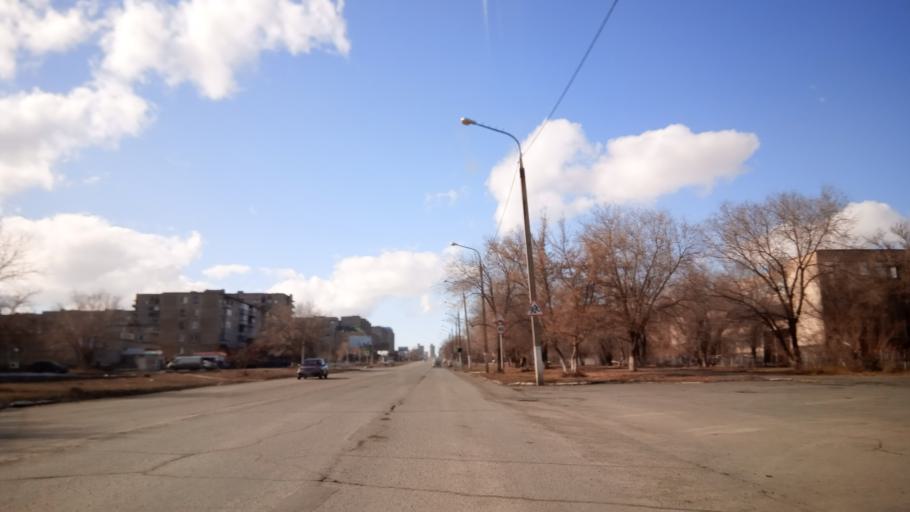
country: RU
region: Orenburg
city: Novotroitsk
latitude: 51.1840
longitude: 58.2826
